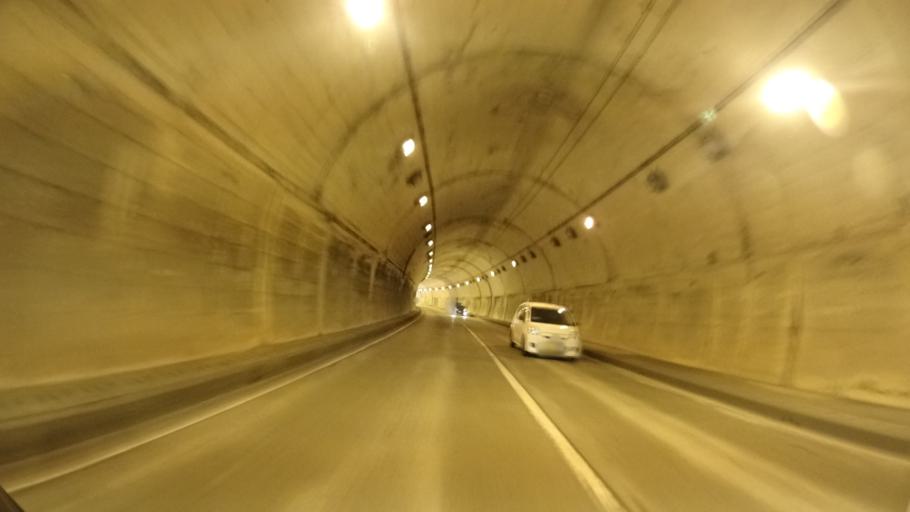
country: JP
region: Ehime
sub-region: Nishiuwa-gun
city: Ikata-cho
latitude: 33.4826
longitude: 132.3249
